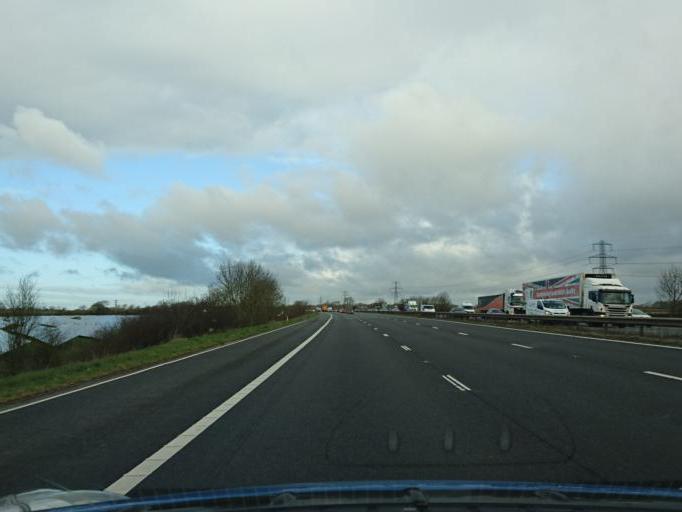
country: GB
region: England
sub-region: Wiltshire
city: Lydiard Tregoze
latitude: 51.5512
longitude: -1.8680
